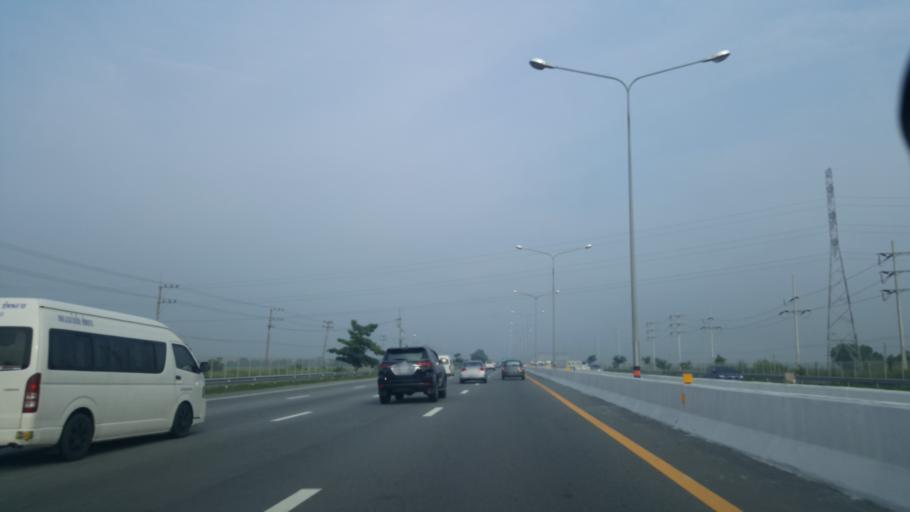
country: TH
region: Chachoengsao
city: Bang Pakong
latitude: 13.5782
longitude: 100.9761
